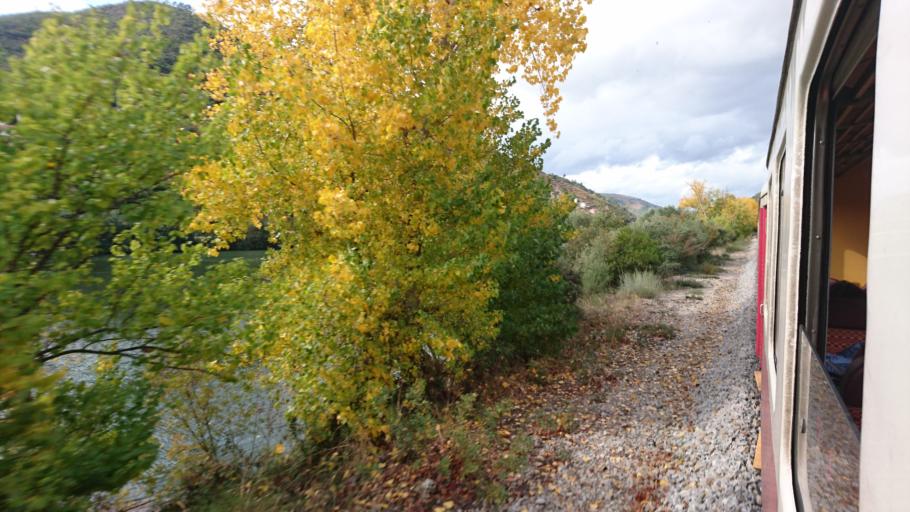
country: PT
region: Viseu
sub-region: Armamar
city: Armamar
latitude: 41.1428
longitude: -7.6992
